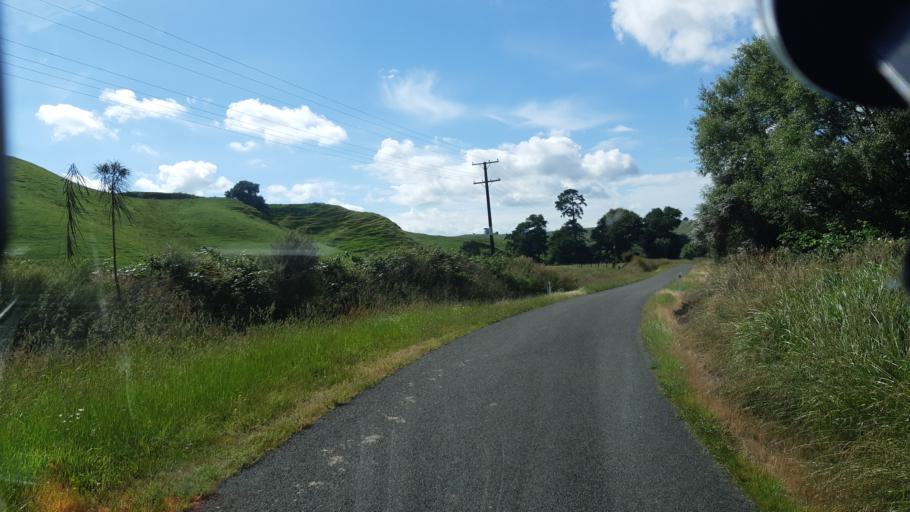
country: NZ
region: Manawatu-Wanganui
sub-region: Rangitikei District
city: Bulls
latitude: -39.9627
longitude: 175.5158
